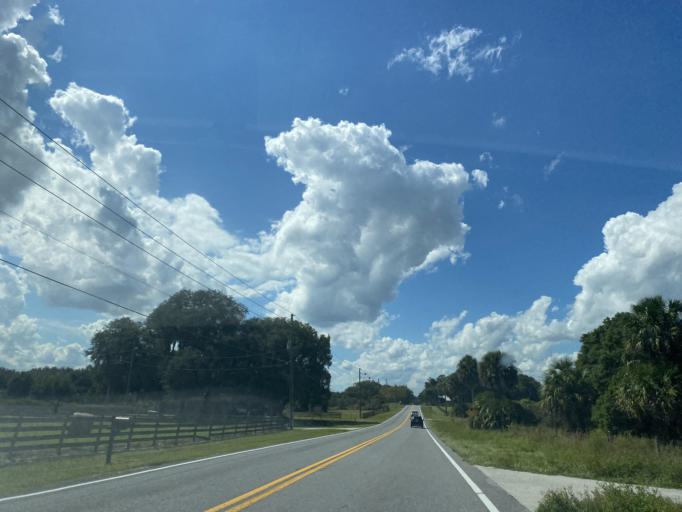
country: US
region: Florida
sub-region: Sumter County
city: The Villages
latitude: 28.9819
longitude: -81.9176
